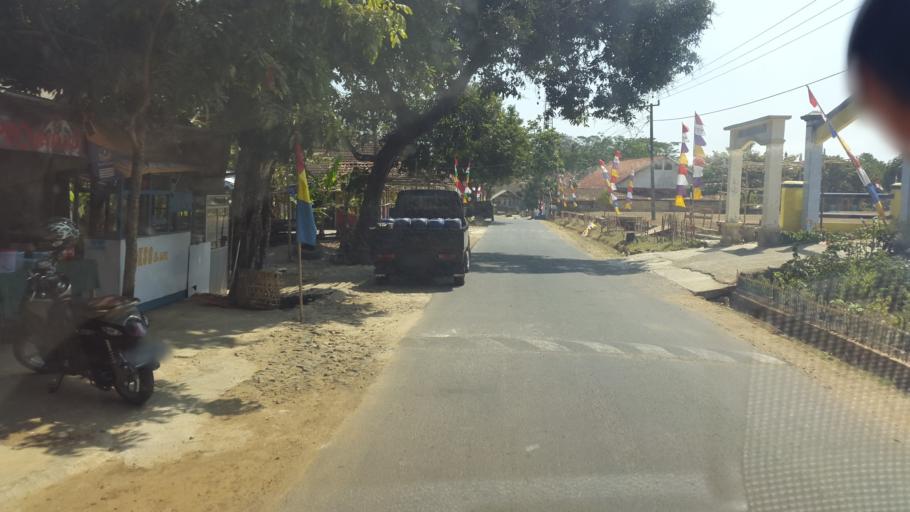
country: ID
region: West Java
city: Gunungbatu
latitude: -7.3348
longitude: 106.4423
